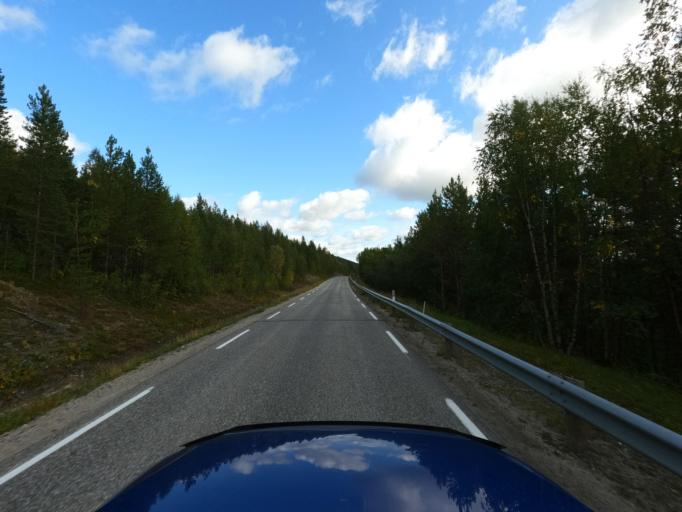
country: NO
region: Finnmark Fylke
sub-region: Karasjok
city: Karasjohka
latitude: 69.4531
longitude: 25.3779
